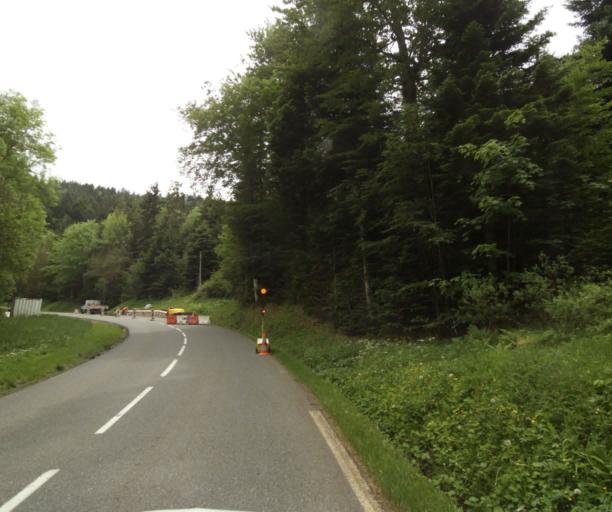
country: FR
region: Rhone-Alpes
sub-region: Departement de la Haute-Savoie
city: Perrignier
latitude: 46.2608
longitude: 6.4475
